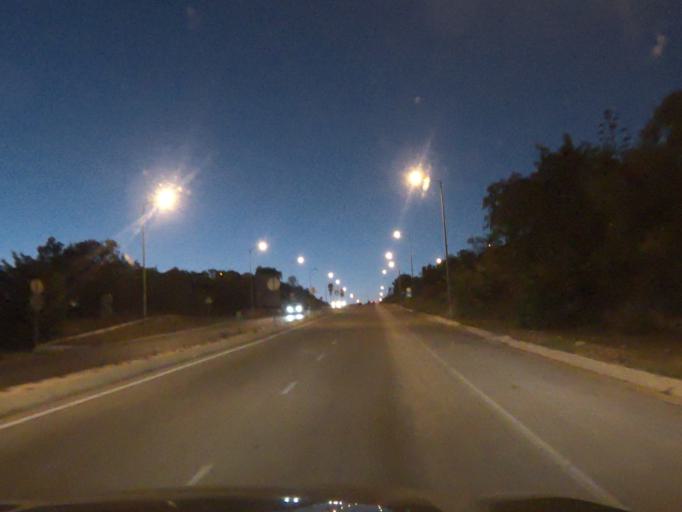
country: PT
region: Faro
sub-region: Faro
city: Santa Barbara de Nexe
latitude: 37.1036
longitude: -7.9994
